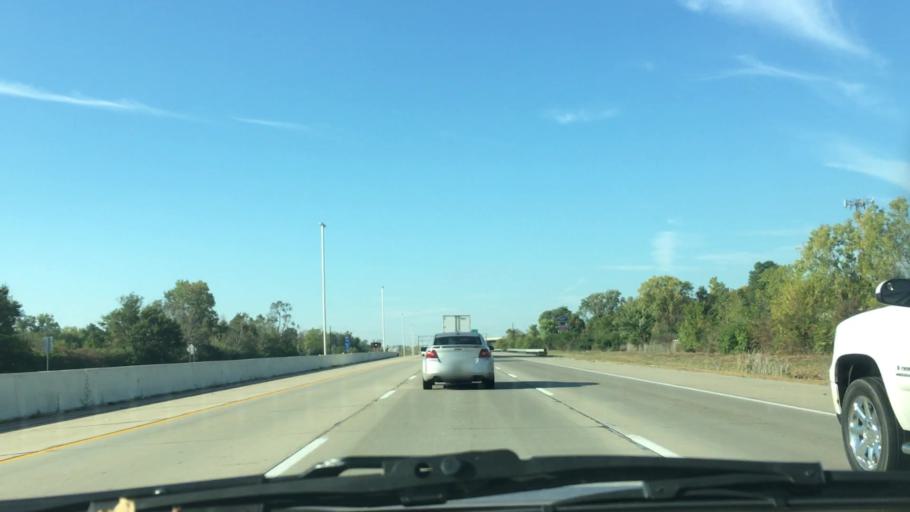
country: US
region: Indiana
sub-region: Marion County
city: Speedway
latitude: 39.7198
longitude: -86.2561
